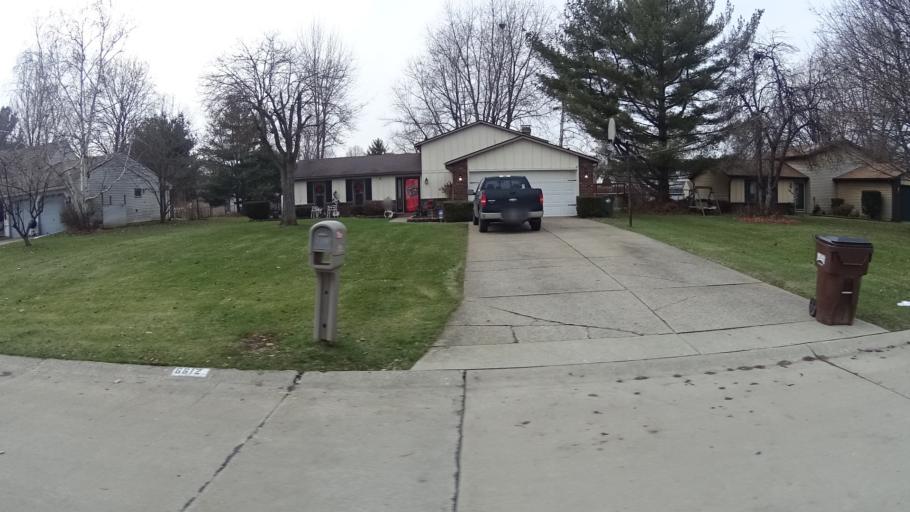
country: US
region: Ohio
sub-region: Lorain County
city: Amherst
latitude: 41.4033
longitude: -82.1850
